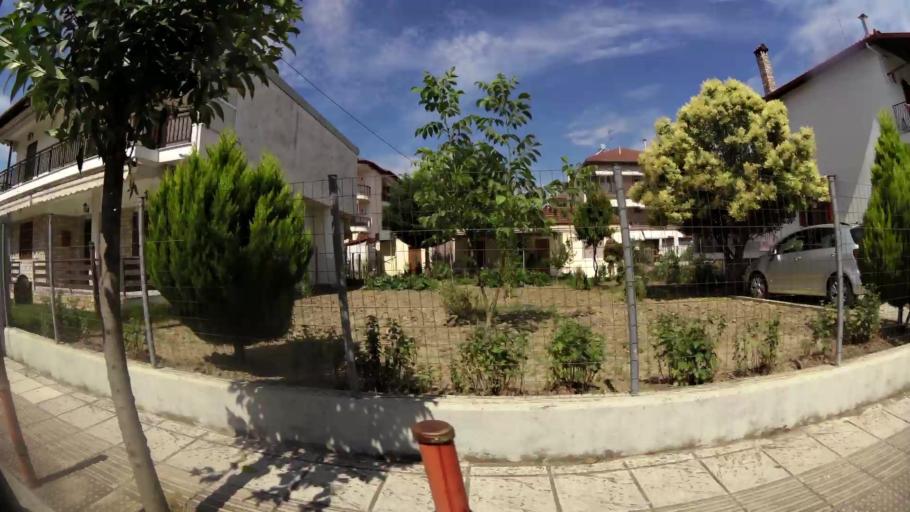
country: GR
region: Central Macedonia
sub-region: Nomos Pierias
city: Katerini
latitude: 40.2656
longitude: 22.4965
